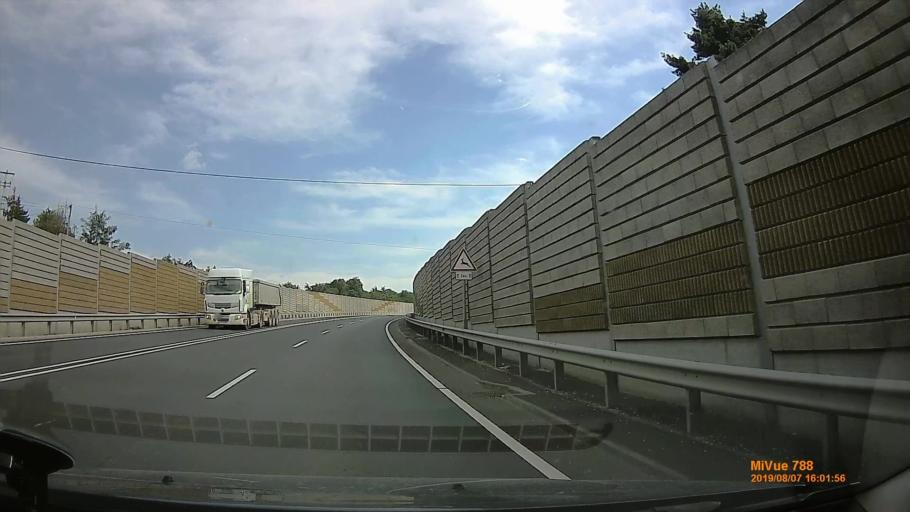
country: HU
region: Vas
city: Kormend
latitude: 46.9848
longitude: 16.6235
